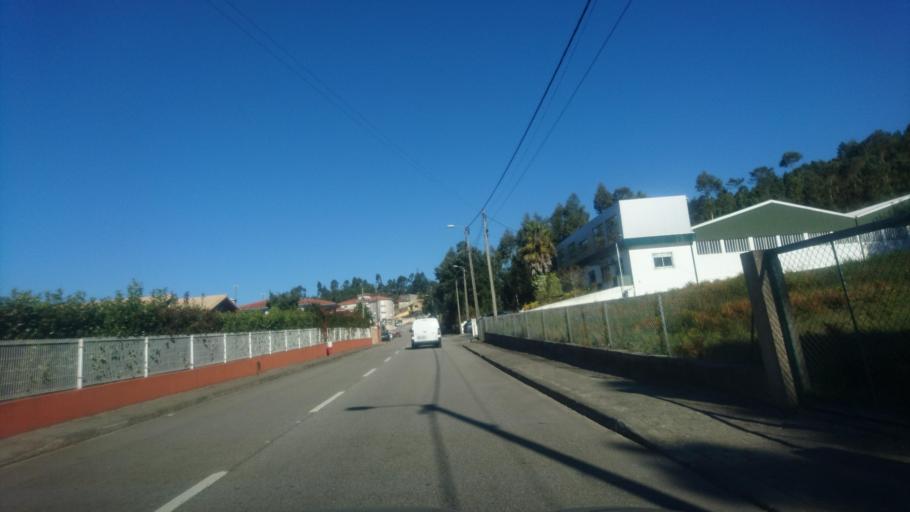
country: PT
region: Aveiro
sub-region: Oliveira de Azemeis
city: Sao Roque
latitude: 40.8787
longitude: -8.4637
